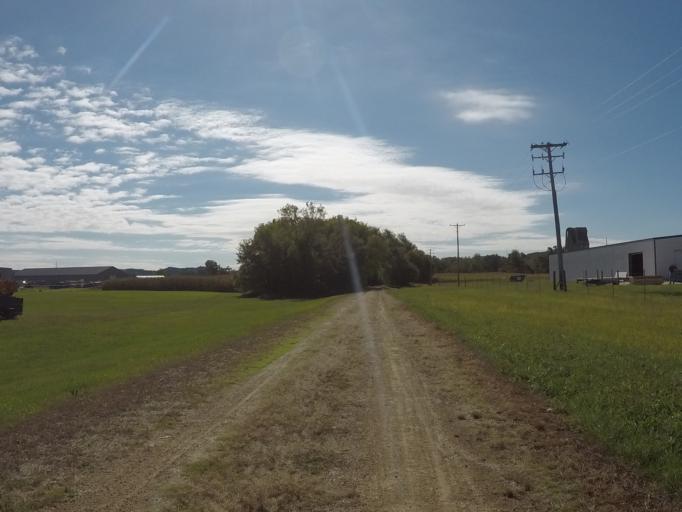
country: US
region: Wisconsin
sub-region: Richland County
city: Richland Center
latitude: 43.2925
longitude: -90.3272
